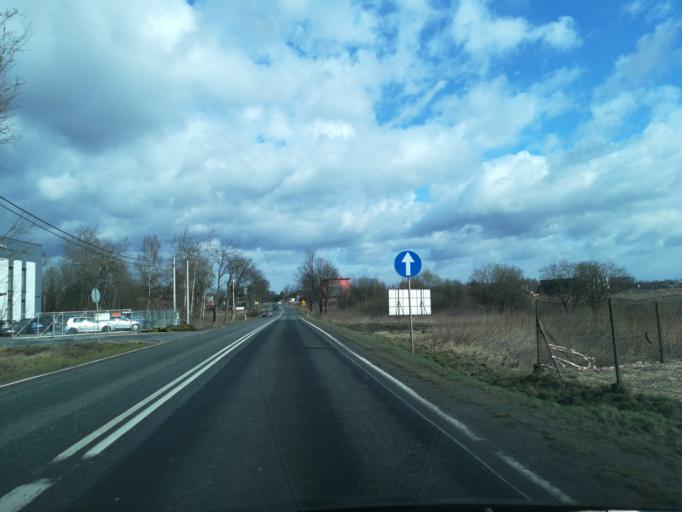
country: PL
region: Lesser Poland Voivodeship
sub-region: Powiat krakowski
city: Kryspinow
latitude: 50.0551
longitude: 19.8018
